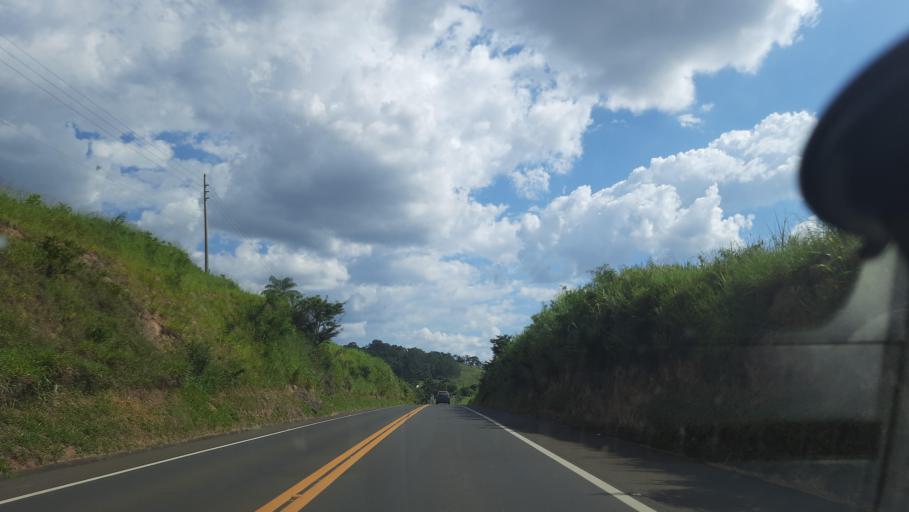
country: BR
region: Sao Paulo
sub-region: Sao Jose Do Rio Pardo
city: Sao Jose do Rio Pardo
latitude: -21.6467
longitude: -46.9088
